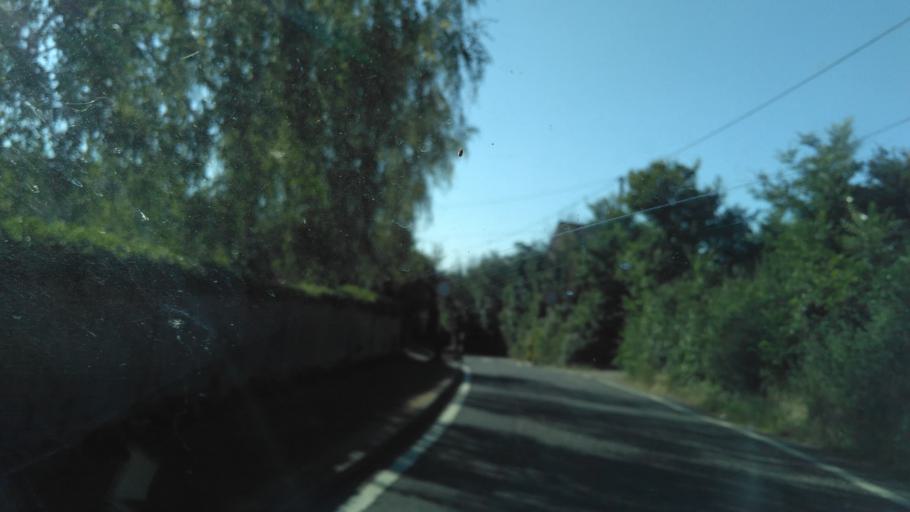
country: GB
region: England
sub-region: Kent
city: Whitstable
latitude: 51.3412
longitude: 1.0059
